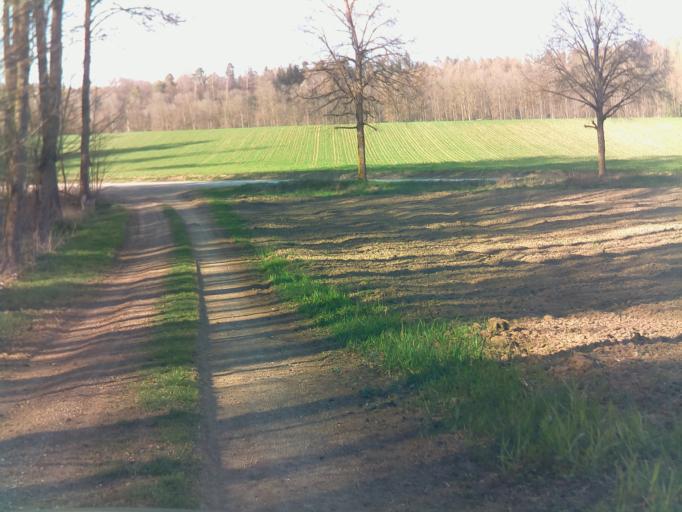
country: DE
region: Bavaria
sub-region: Swabia
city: Pottmes
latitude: 48.5895
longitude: 11.0740
